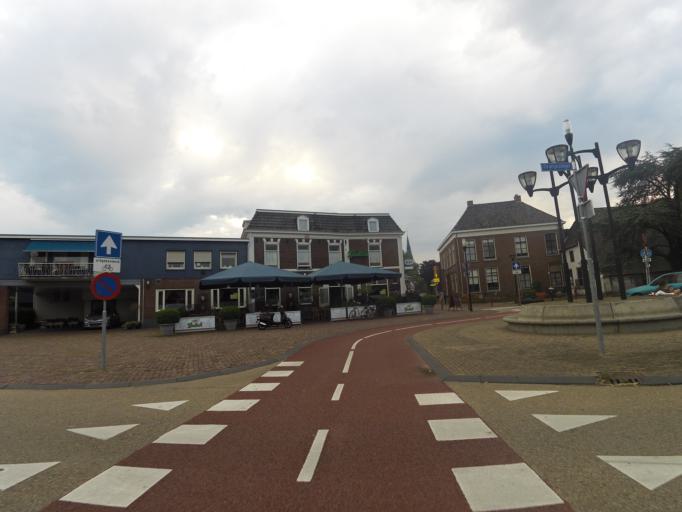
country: NL
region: Gelderland
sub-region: Oude IJsselstreek
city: Gendringen
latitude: 51.8710
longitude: 6.3797
